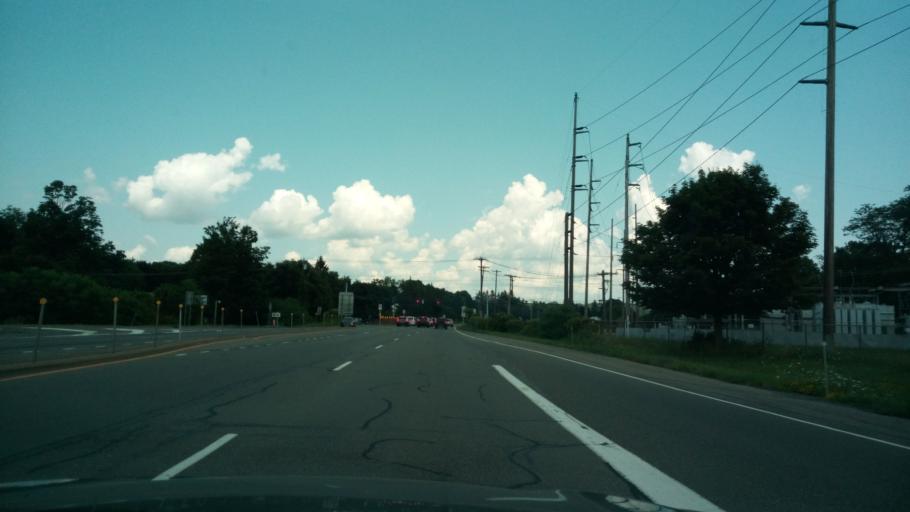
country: US
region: New York
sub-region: Chemung County
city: Horseheads
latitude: 42.1635
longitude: -76.8394
